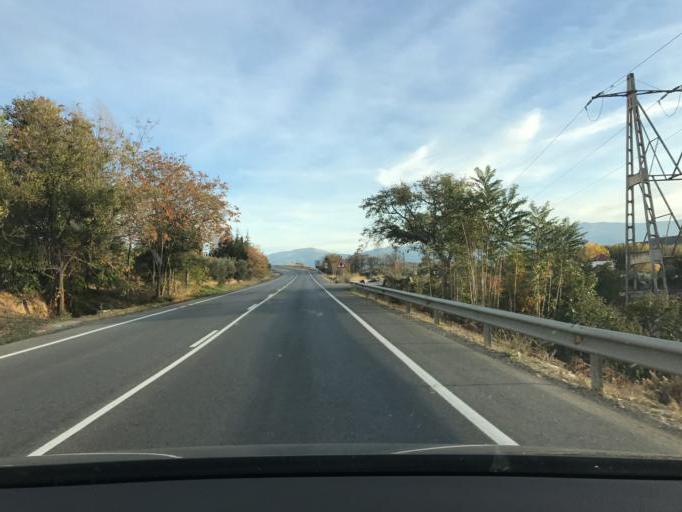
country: ES
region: Andalusia
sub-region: Provincia de Granada
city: Guadix
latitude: 37.2776
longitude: -3.1117
